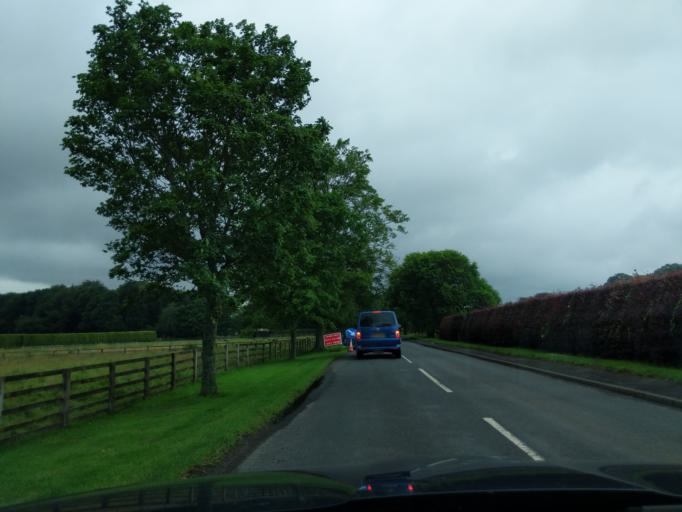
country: GB
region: England
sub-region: Northumberland
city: Ford
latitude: 55.6456
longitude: -2.1134
